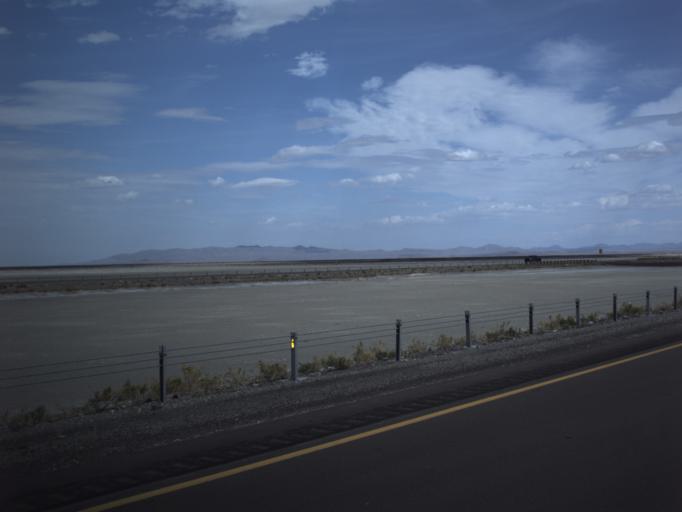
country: US
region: Utah
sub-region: Tooele County
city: Wendover
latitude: 40.7279
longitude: -113.3611
